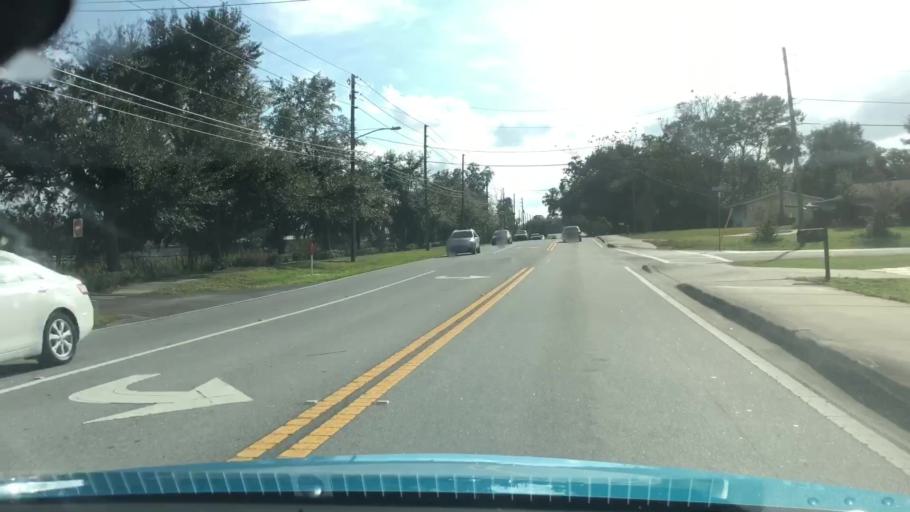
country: US
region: Florida
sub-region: Seminole County
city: Longwood
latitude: 28.7295
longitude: -81.3351
